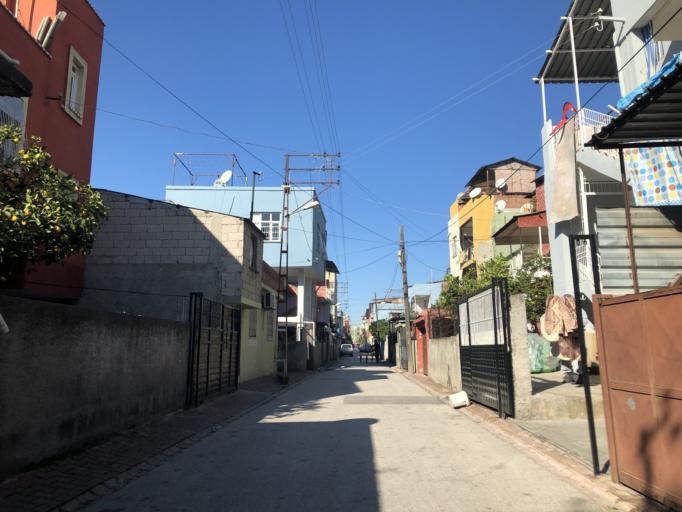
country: TR
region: Adana
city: Yuregir
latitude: 37.0064
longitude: 35.3675
